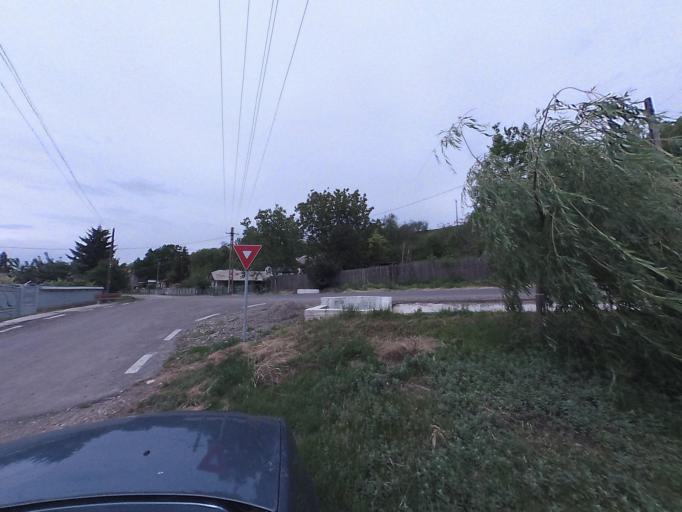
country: RO
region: Neamt
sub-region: Comuna Dulcesti
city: Dulcesti
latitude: 46.9555
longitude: 26.7991
